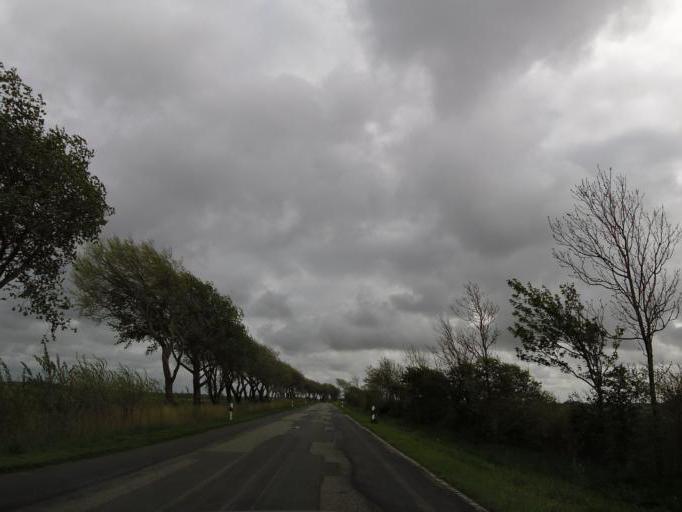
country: DE
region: Schleswig-Holstein
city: Galmsbull
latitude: 54.7670
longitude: 8.7516
